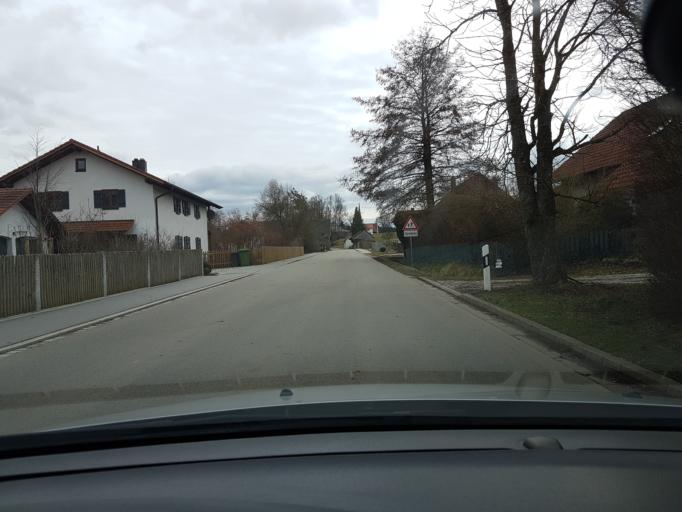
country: DE
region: Bavaria
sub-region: Lower Bavaria
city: Eging
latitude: 48.4960
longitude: 12.2094
